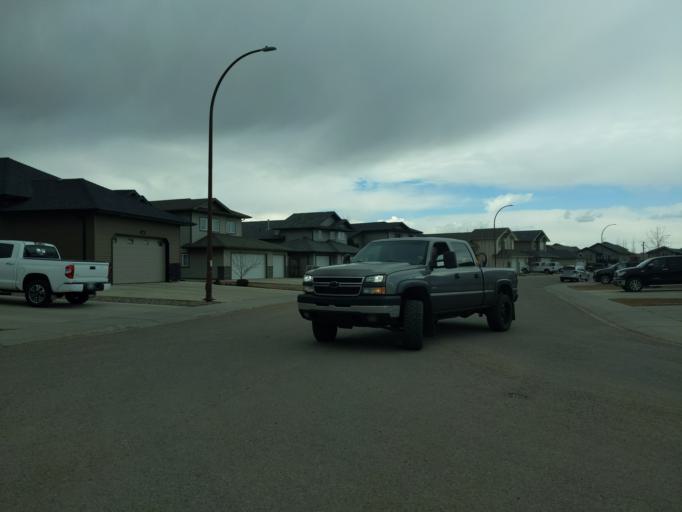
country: CA
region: Saskatchewan
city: Lloydminster
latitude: 53.2737
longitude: -110.0513
